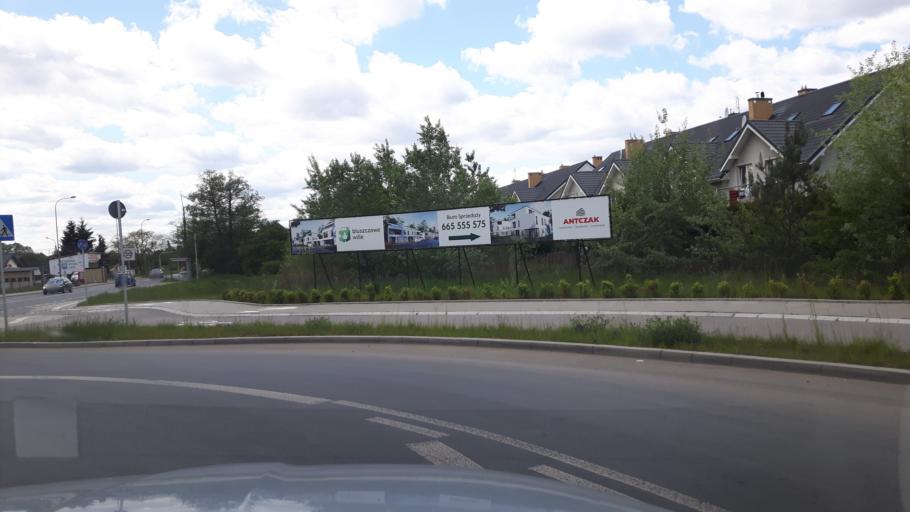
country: PL
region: Masovian Voivodeship
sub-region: Powiat legionowski
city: Stanislawow Pierwszy
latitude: 52.3404
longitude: 21.0503
